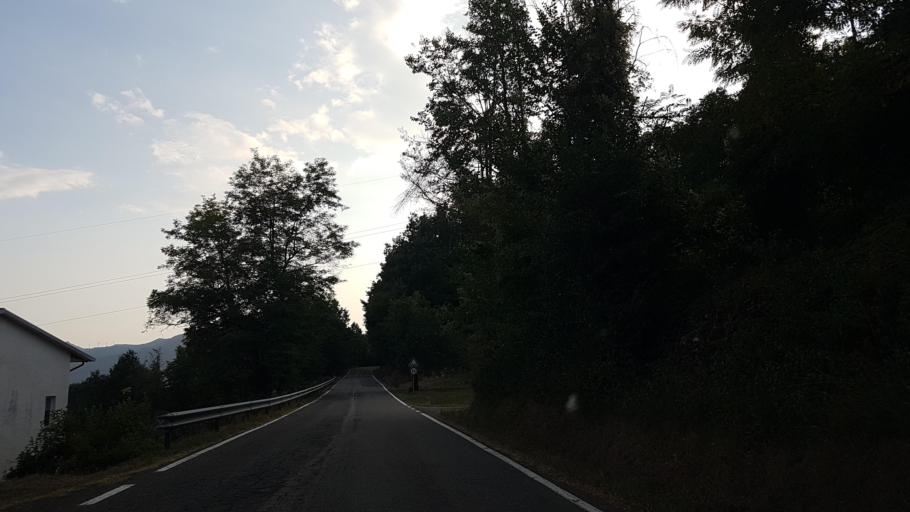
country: IT
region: Emilia-Romagna
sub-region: Provincia di Parma
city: Albareto
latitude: 44.4665
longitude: 9.7036
